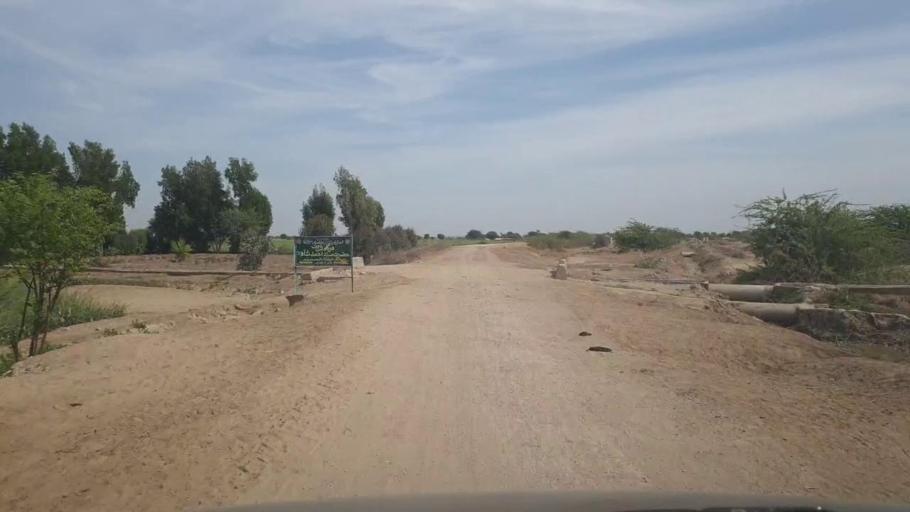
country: PK
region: Sindh
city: Kunri
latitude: 25.2400
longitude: 69.6404
